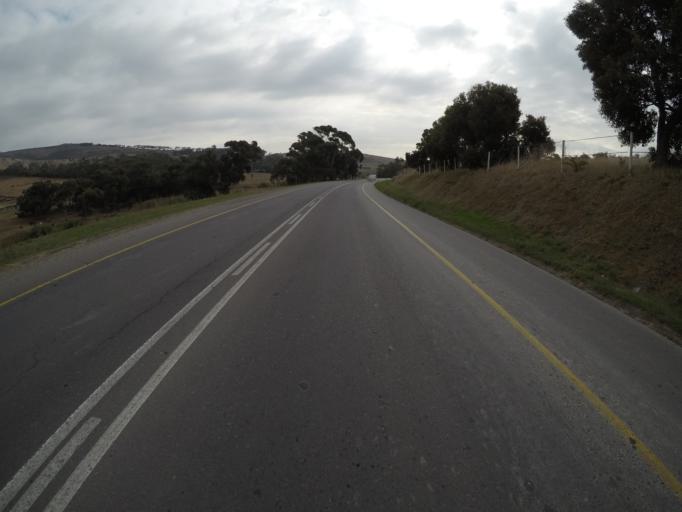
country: ZA
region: Western Cape
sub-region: City of Cape Town
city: Sunset Beach
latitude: -33.8252
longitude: 18.5844
